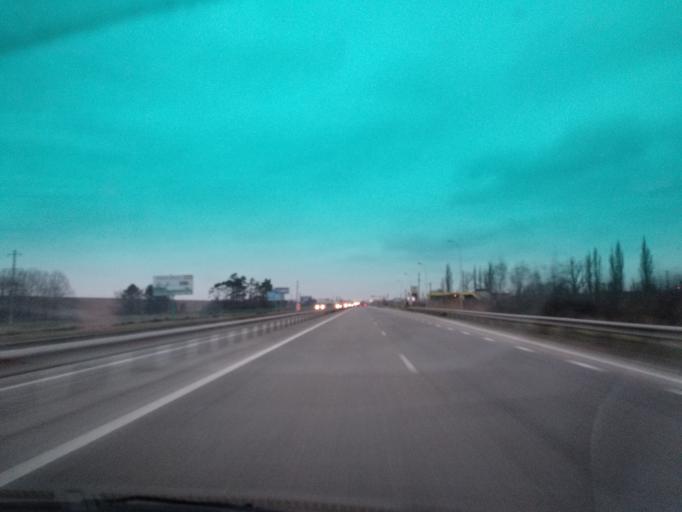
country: RU
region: Adygeya
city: Tlyustenkhabl'
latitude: 44.9289
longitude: 39.1390
